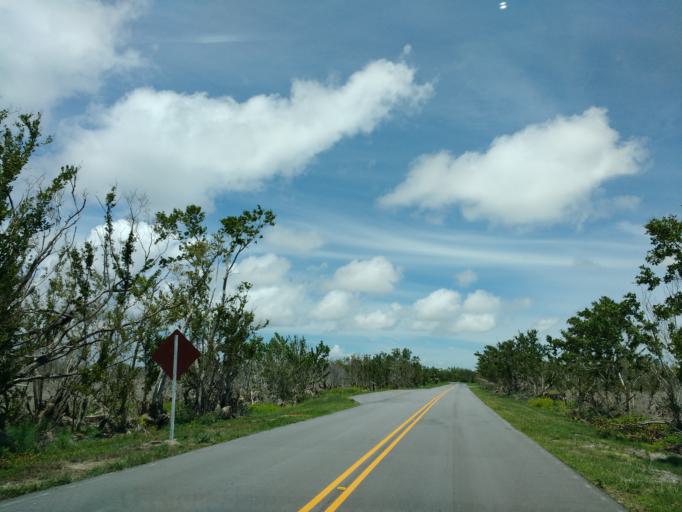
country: US
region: Florida
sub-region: Monroe County
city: Islamorada
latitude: 25.1389
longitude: -80.9351
